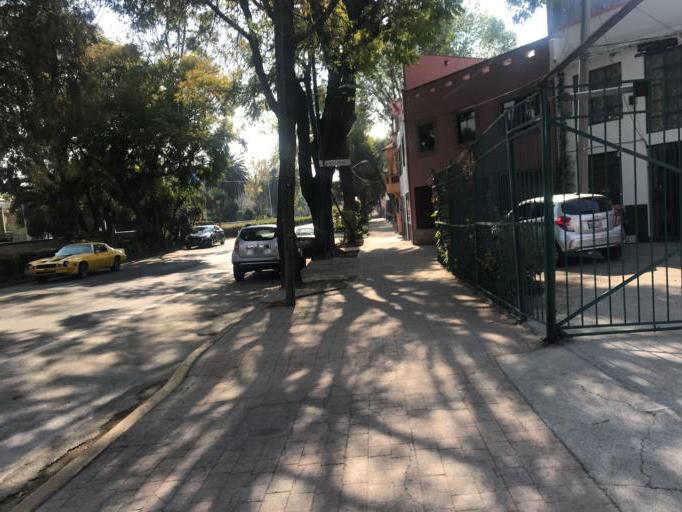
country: MX
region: Mexico City
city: Cuauhtemoc
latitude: 19.4563
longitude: -99.1701
